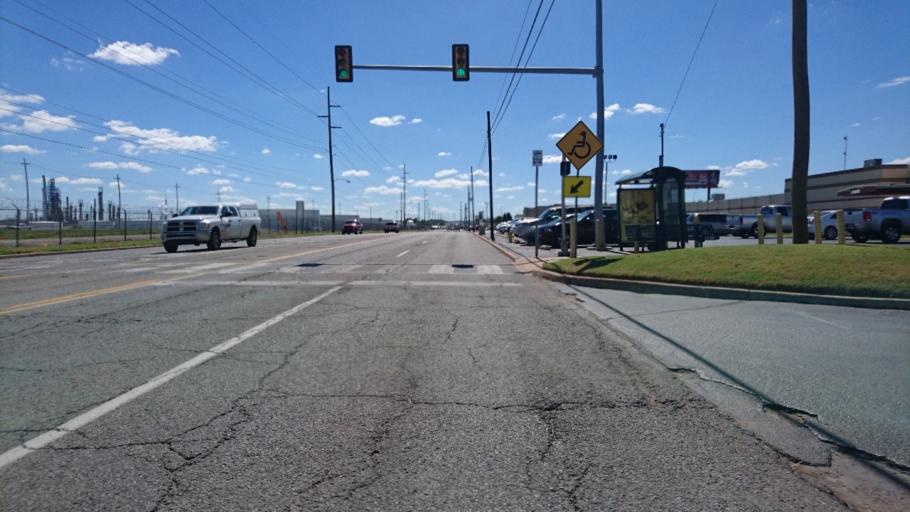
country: US
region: Oklahoma
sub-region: Tulsa County
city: Tulsa
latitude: 36.1217
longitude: -96.0072
